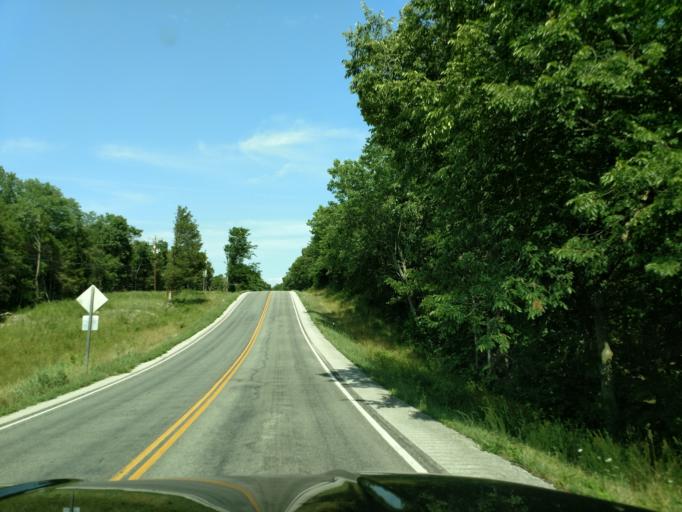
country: US
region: Missouri
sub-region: Barry County
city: Shell Knob
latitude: 36.6097
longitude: -93.5860
